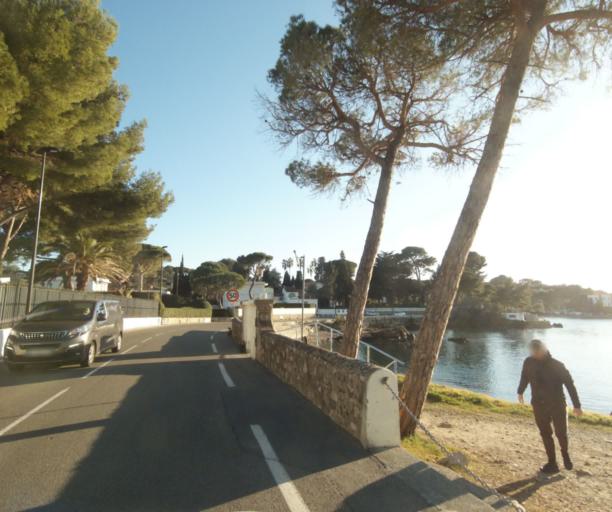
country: FR
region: Provence-Alpes-Cote d'Azur
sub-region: Departement des Alpes-Maritimes
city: Antibes
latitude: 43.5531
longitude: 7.1222
